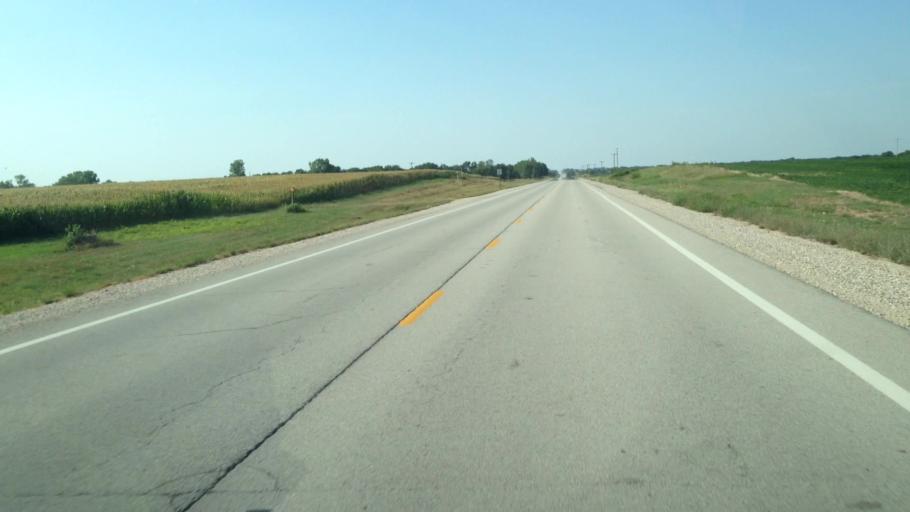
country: US
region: Kansas
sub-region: Anderson County
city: Garnett
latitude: 38.0924
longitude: -95.2431
